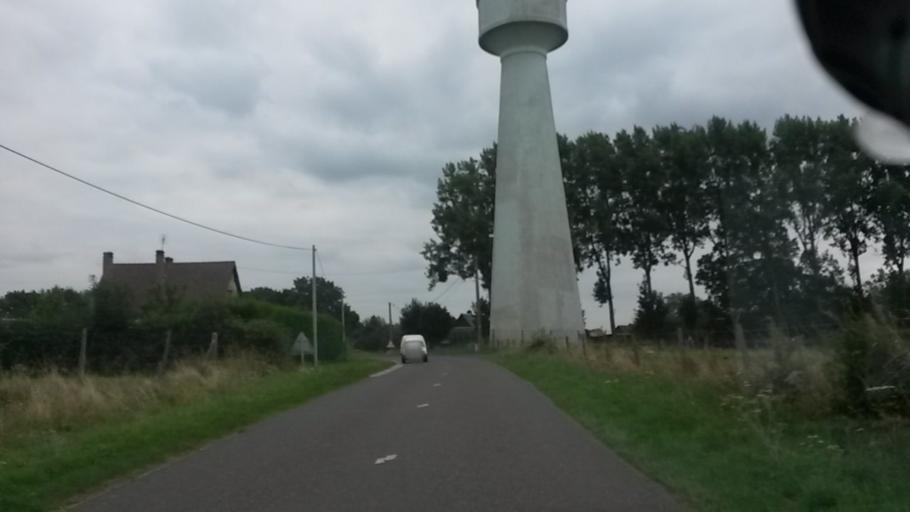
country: FR
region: Haute-Normandie
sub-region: Departement de la Seine-Maritime
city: La Feuillie
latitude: 49.4733
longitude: 1.5292
